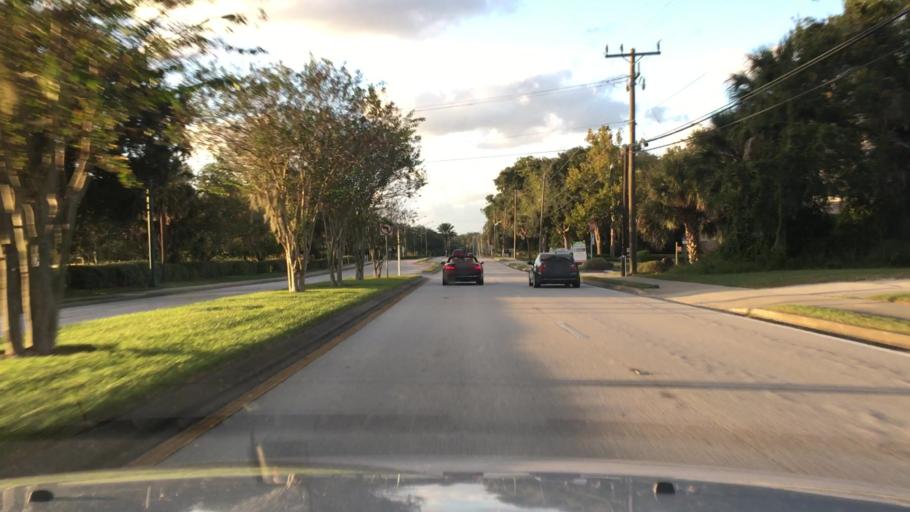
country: US
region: Florida
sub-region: Volusia County
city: Ormond Beach
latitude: 29.2879
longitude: -81.0846
